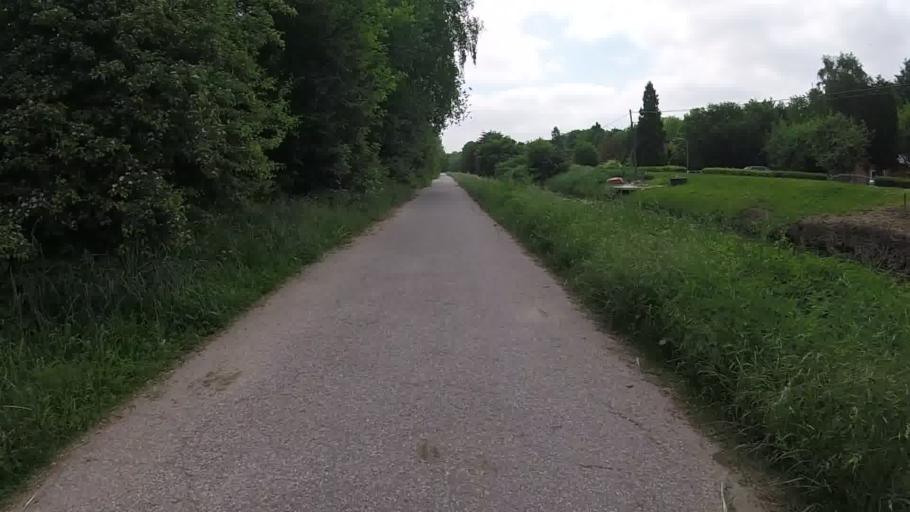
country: DE
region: Schleswig-Holstein
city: Oststeinbek
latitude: 53.4975
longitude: 10.1344
